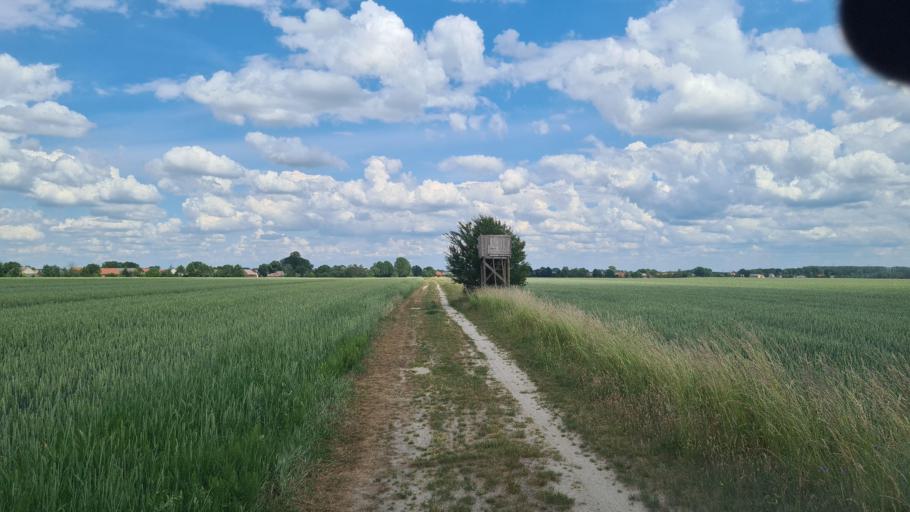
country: DE
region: Brandenburg
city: Doberlug-Kirchhain
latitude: 51.6487
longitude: 13.5183
